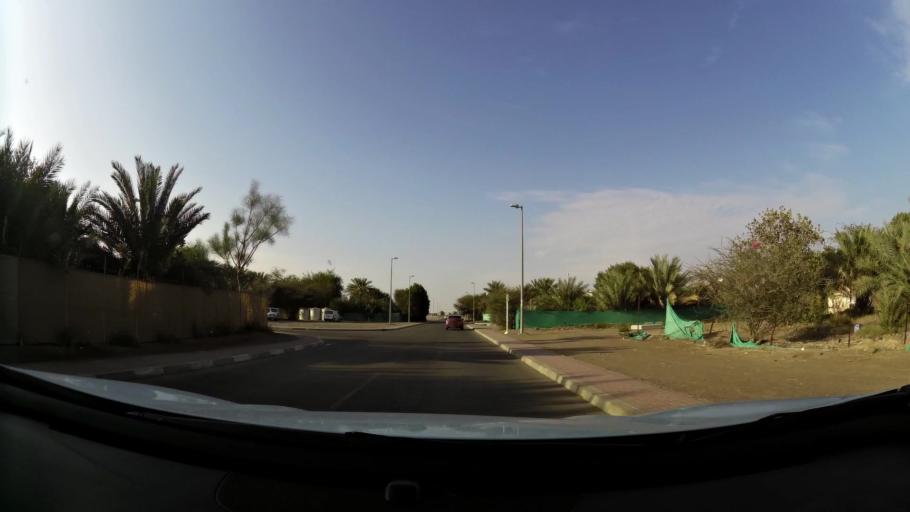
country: AE
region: Abu Dhabi
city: Al Ain
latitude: 24.0849
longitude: 55.8426
